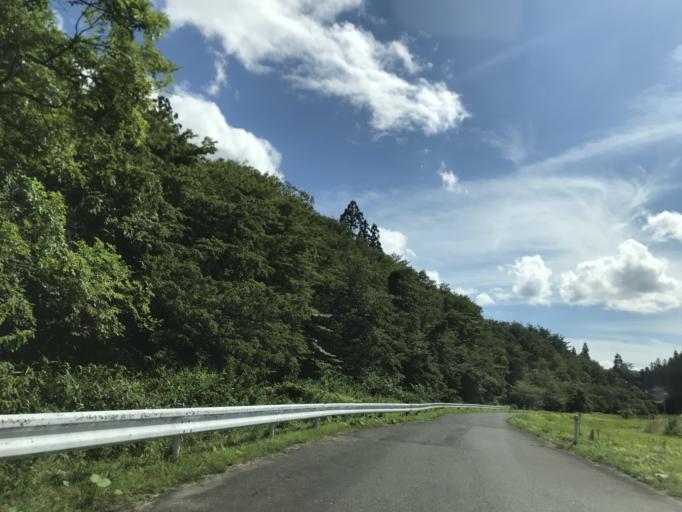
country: JP
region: Iwate
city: Ichinoseki
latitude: 38.9605
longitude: 140.9487
